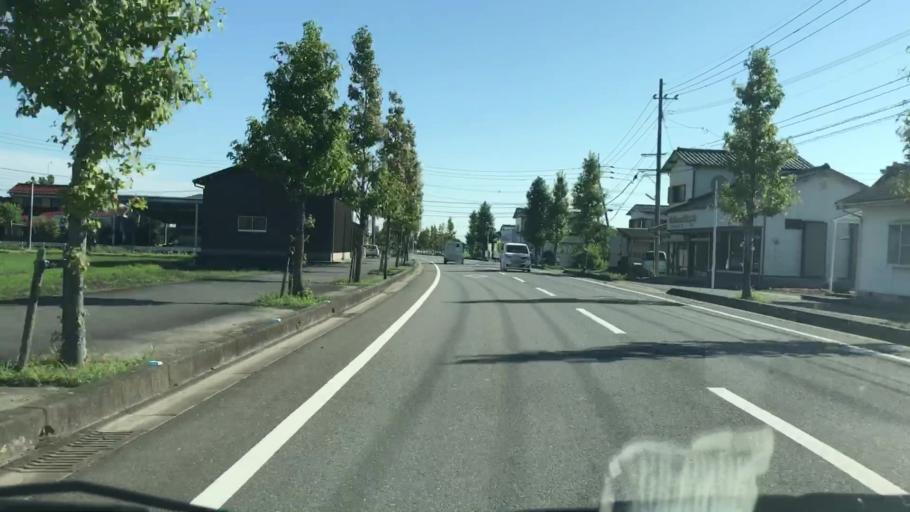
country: JP
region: Saga Prefecture
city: Okawa
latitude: 33.1893
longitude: 130.3145
